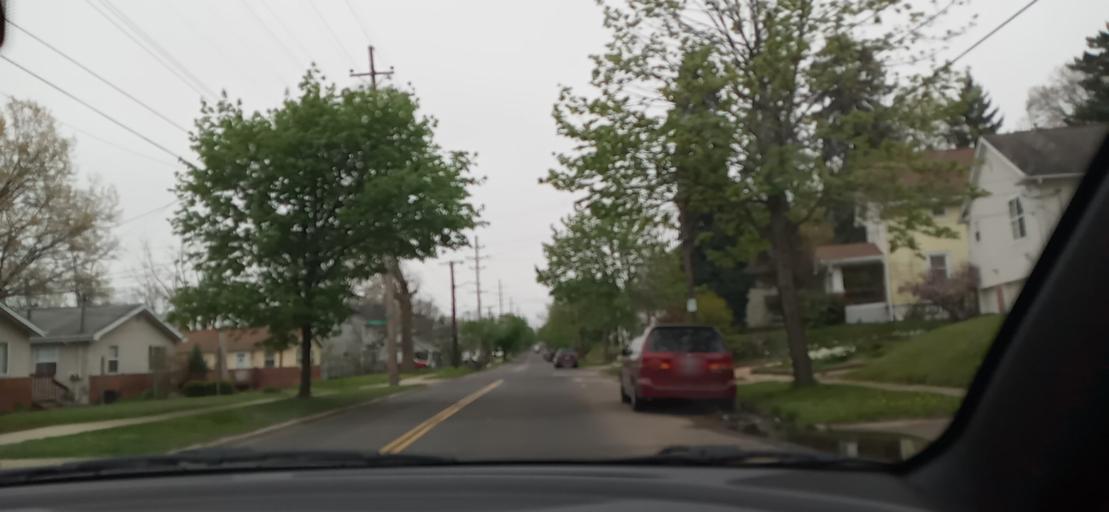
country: US
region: Ohio
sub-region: Summit County
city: Akron
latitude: 41.0548
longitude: -81.5495
